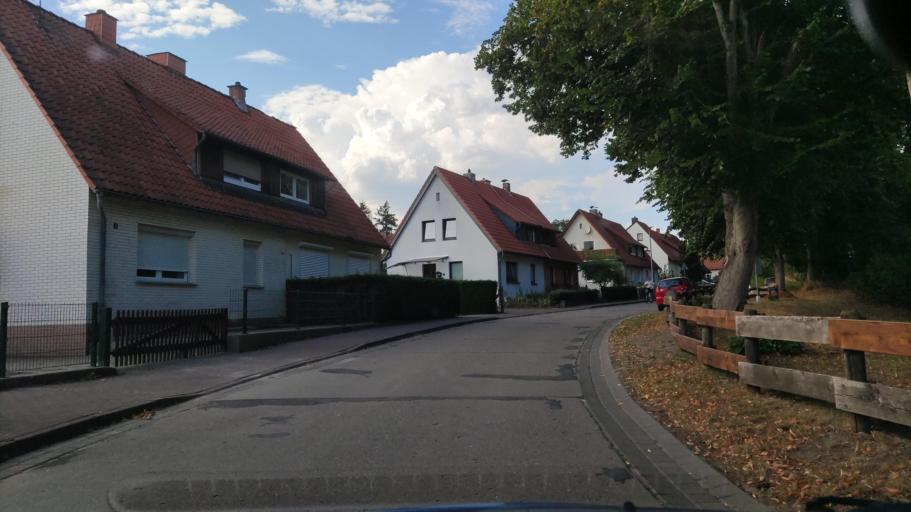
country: DE
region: Lower Saxony
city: Hitzacker
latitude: 53.1525
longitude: 11.0365
